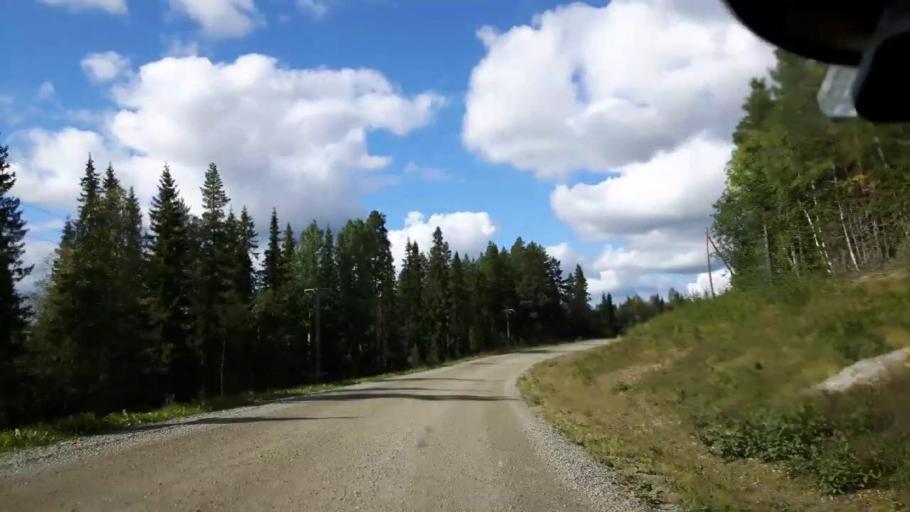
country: SE
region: Jaemtland
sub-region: Stroemsunds Kommun
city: Stroemsund
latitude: 63.3374
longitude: 15.5669
